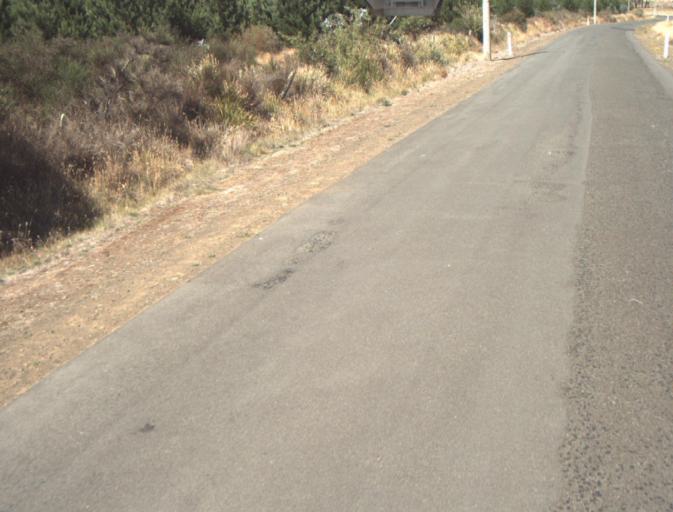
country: AU
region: Tasmania
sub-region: Launceston
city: Newstead
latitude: -41.3302
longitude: 147.3094
